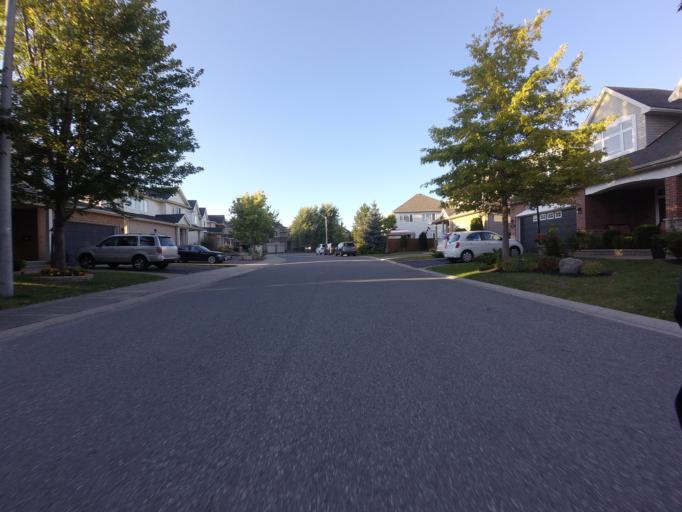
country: CA
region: Ontario
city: Ottawa
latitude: 45.2853
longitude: -75.7044
